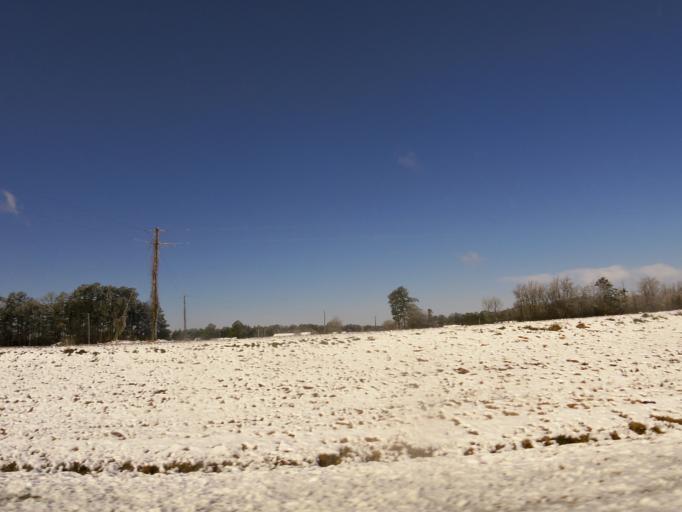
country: US
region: North Carolina
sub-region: Wilson County
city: Elm City
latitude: 35.7957
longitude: -77.8556
